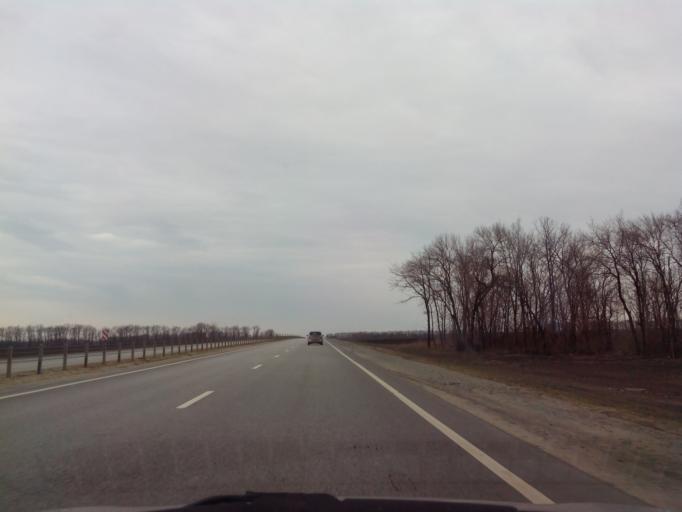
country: RU
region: Tambov
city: Zavoronezhskoye
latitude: 52.8975
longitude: 40.6739
